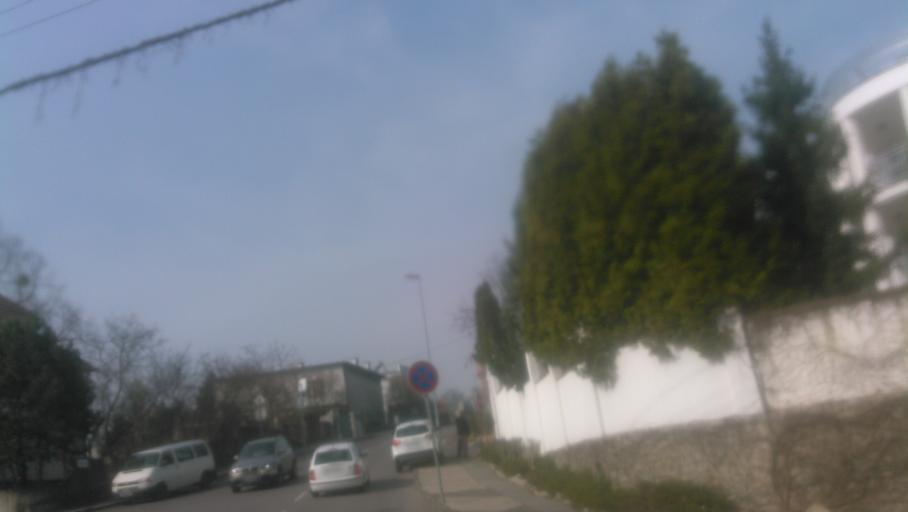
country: SK
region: Bratislavsky
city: Bratislava
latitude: 48.1529
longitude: 17.0979
